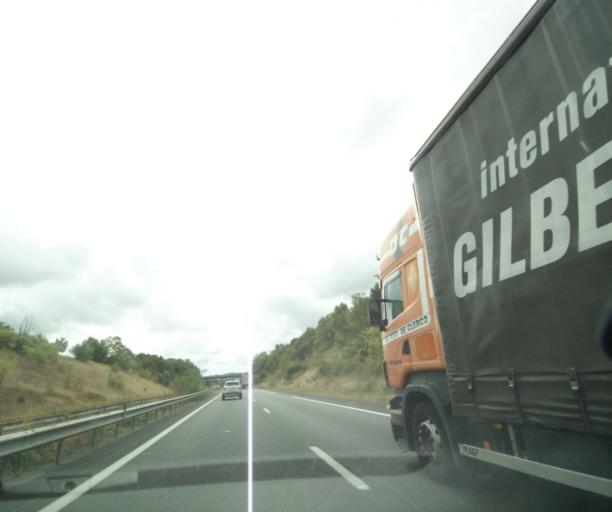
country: FR
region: Poitou-Charentes
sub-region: Departement de la Charente-Maritime
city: Mirambeau
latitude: 45.3771
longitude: -0.5983
